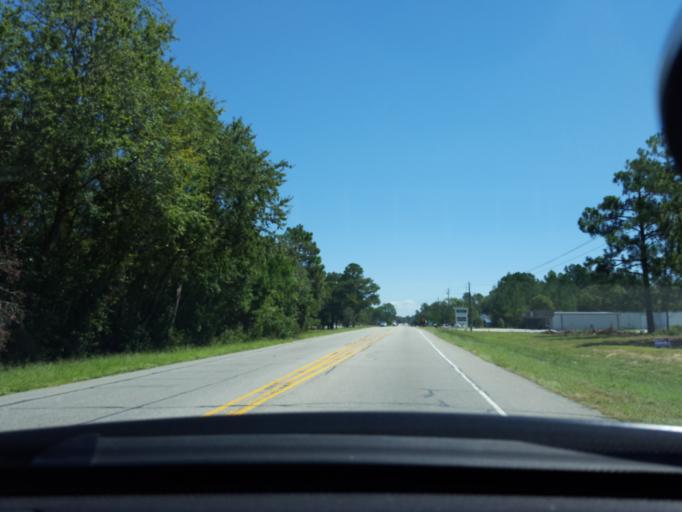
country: US
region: North Carolina
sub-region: Bladen County
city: Elizabethtown
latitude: 34.6471
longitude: -78.5824
